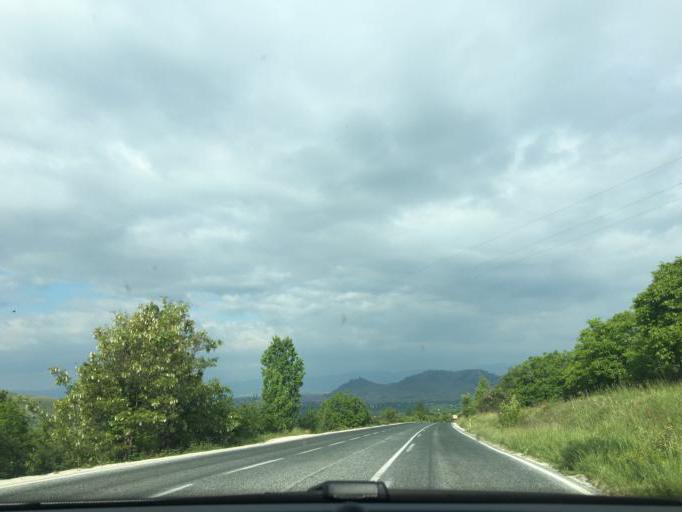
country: MK
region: Prilep
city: Prilep
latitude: 41.3688
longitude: 21.6387
